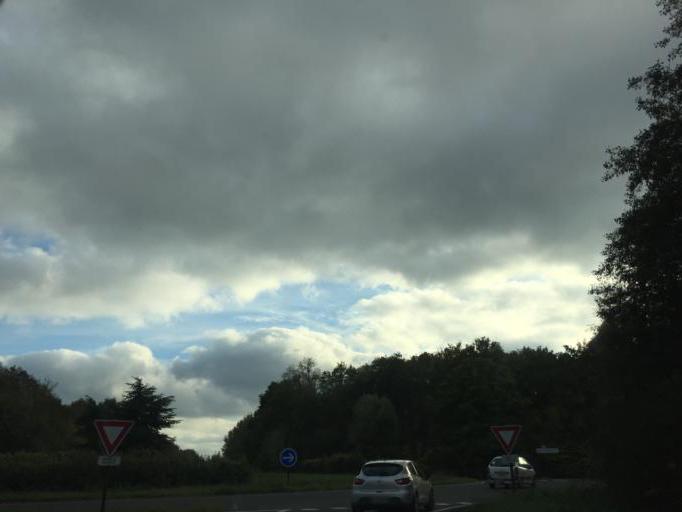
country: FR
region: Ile-de-France
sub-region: Departement de Seine-et-Marne
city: Villeneuve-le-Comte
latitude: 48.8157
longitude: 2.8419
